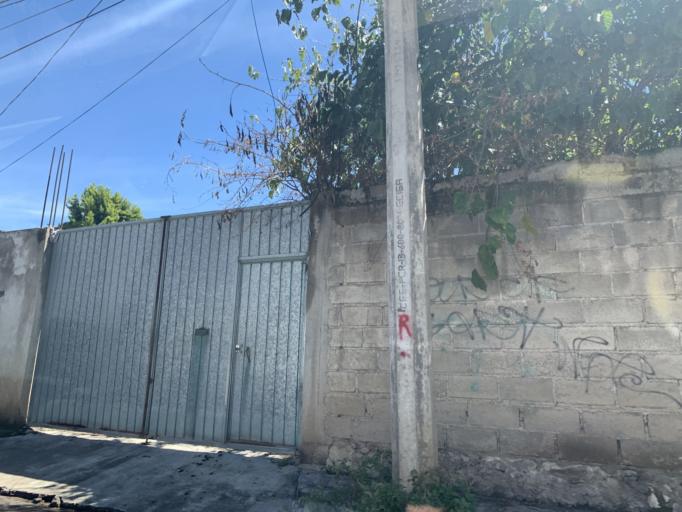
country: MX
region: Puebla
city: Cuautlancingo
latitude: 19.0826
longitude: -98.2692
